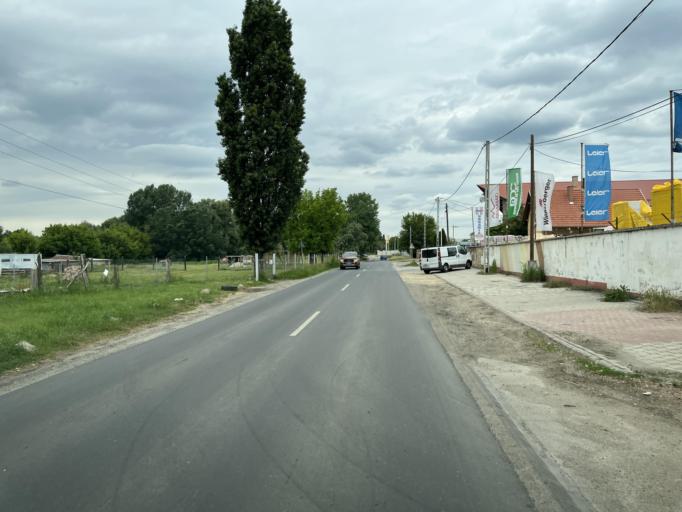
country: HU
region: Pest
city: Nagytarcsa
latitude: 47.5395
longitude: 19.2777
